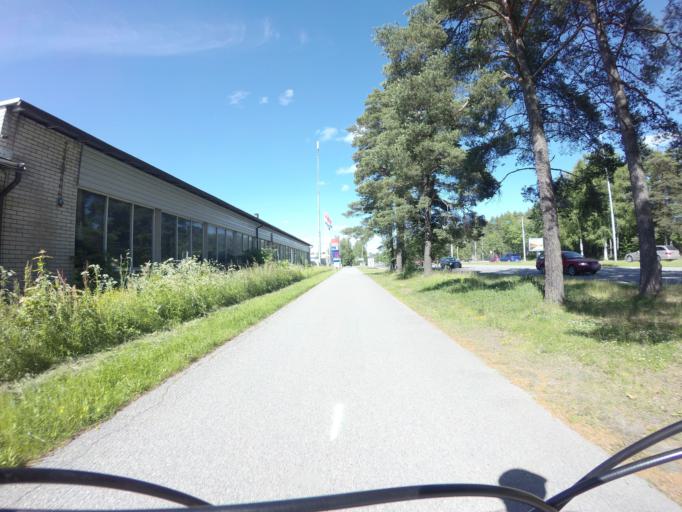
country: FI
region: Varsinais-Suomi
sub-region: Turku
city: Turku
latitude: 60.4823
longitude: 22.2718
